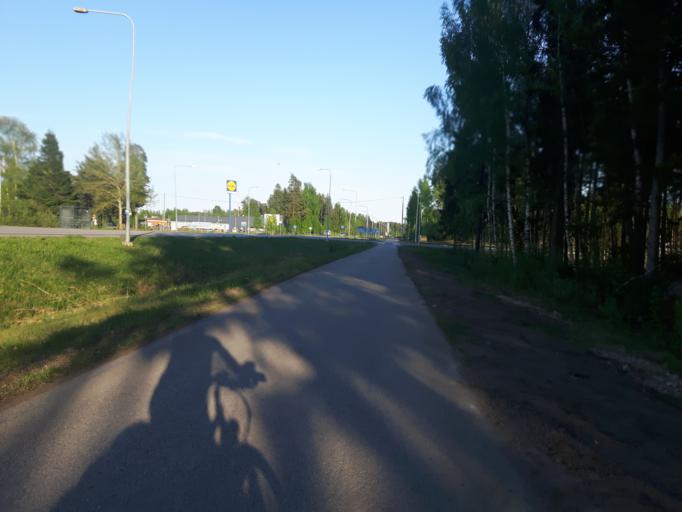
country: FI
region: Uusimaa
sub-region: Loviisa
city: Lovisa
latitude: 60.4573
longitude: 26.1967
